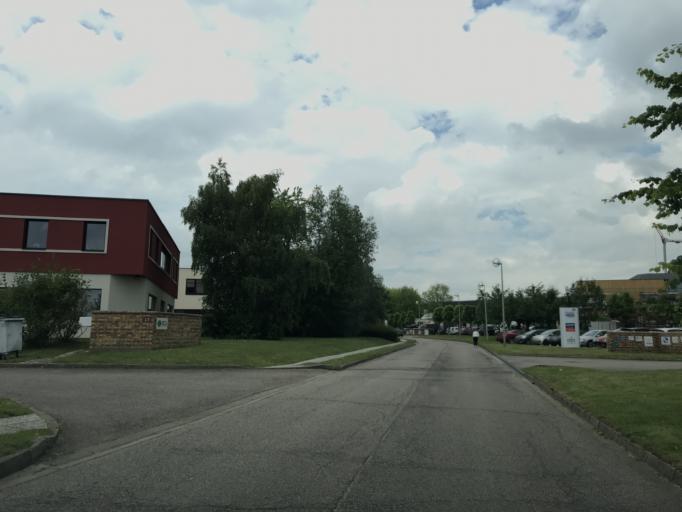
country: FR
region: Haute-Normandie
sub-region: Departement de la Seine-Maritime
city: Mont-Saint-Aignan
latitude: 49.4743
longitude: 1.0968
